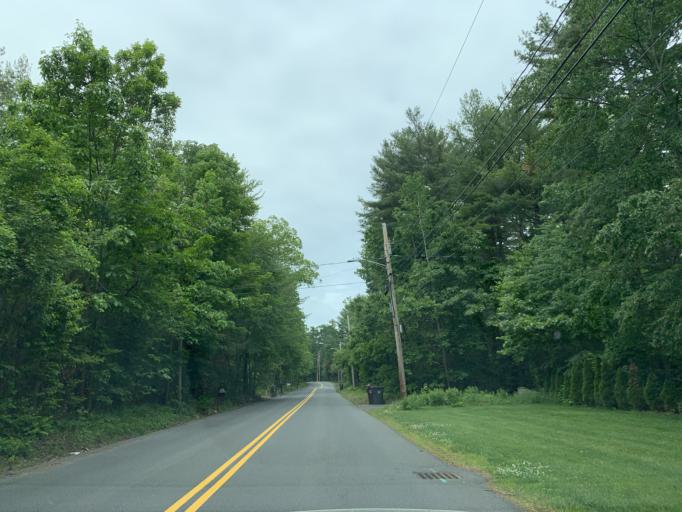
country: US
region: Massachusetts
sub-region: Hampshire County
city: Southampton
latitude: 42.1894
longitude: -72.7665
